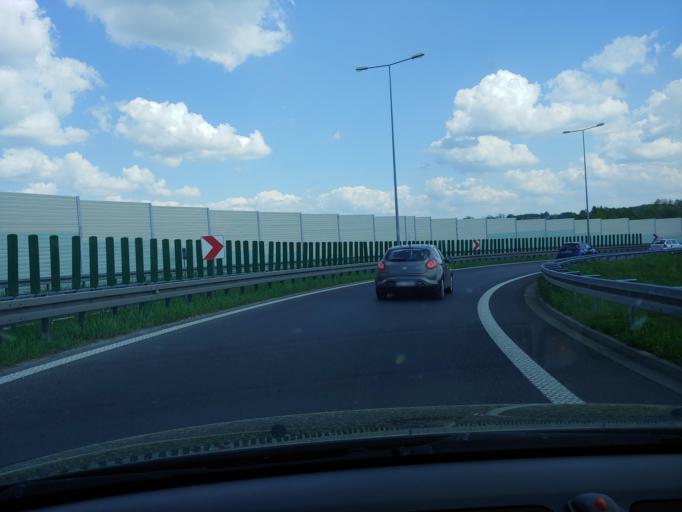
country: PL
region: Lesser Poland Voivodeship
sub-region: Powiat tarnowski
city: Lisia Gora
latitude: 50.0559
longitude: 21.0158
